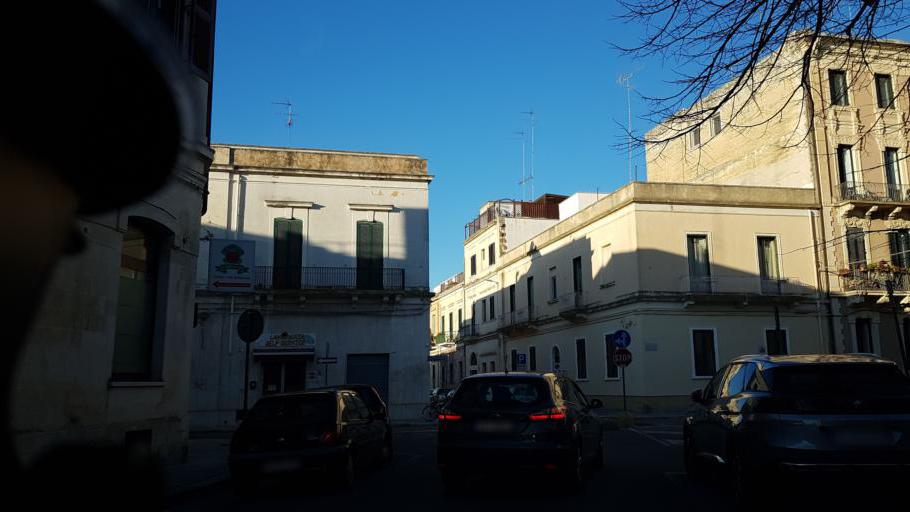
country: IT
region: Apulia
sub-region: Provincia di Lecce
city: Lecce
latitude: 40.3565
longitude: 18.1768
